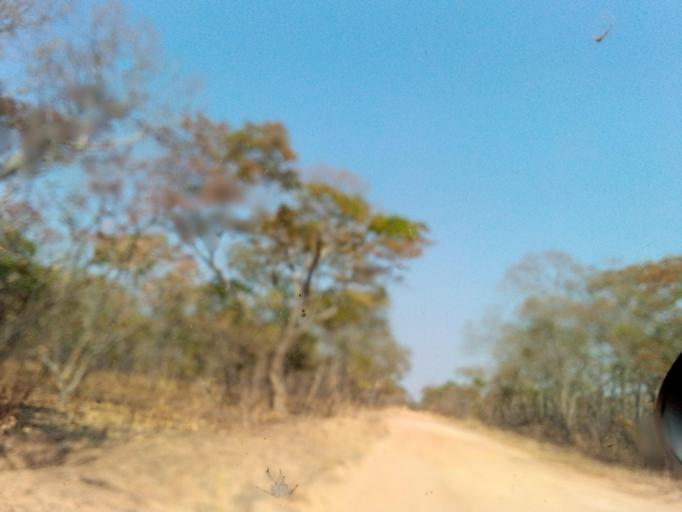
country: ZM
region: Northern
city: Mpika
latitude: -12.2418
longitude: 30.8281
